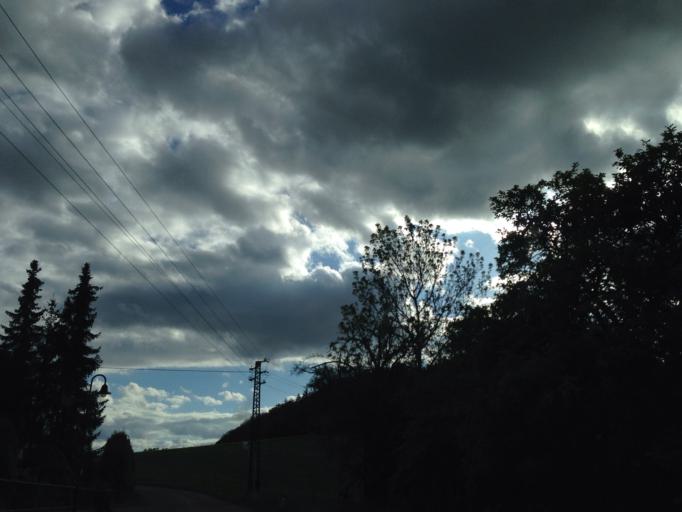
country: DE
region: Thuringia
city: Wernburg
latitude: 50.6759
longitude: 11.5968
